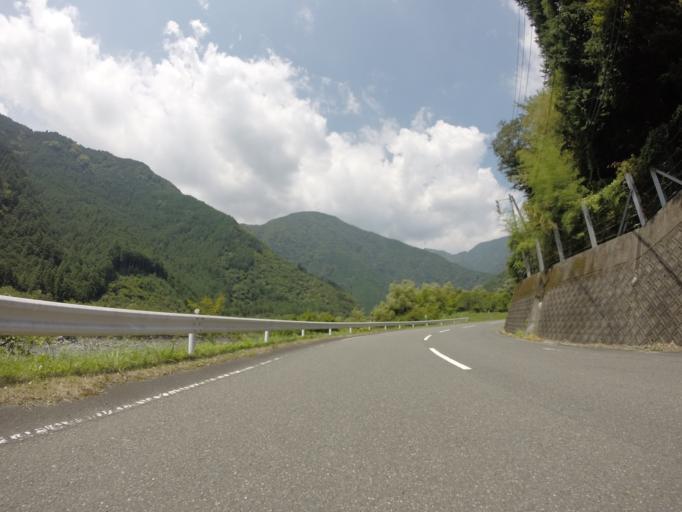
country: JP
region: Shizuoka
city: Shizuoka-shi
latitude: 35.2555
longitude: 138.3336
